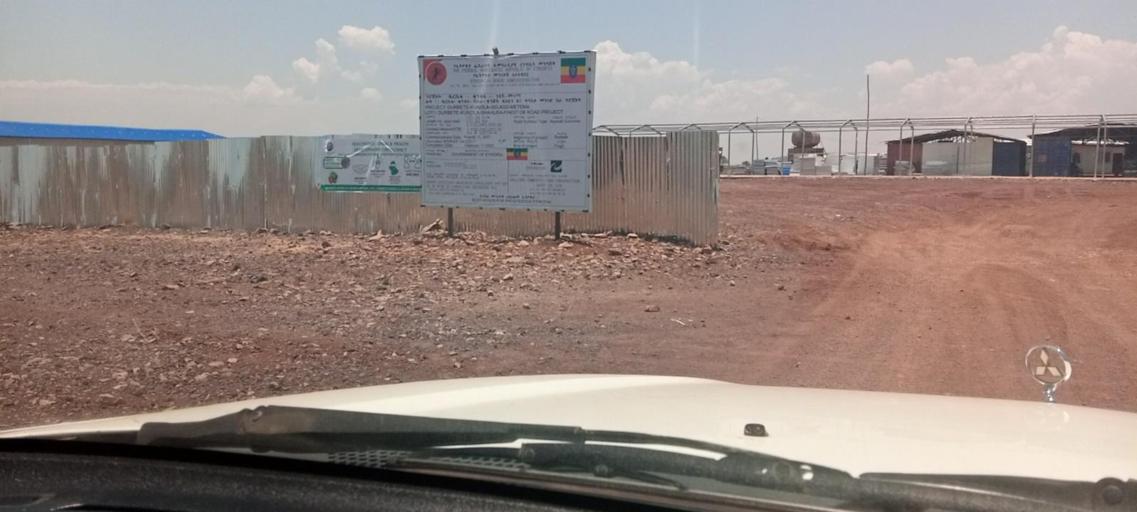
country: ET
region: Amhara
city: Bahir Dar
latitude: 11.8763
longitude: 37.0170
